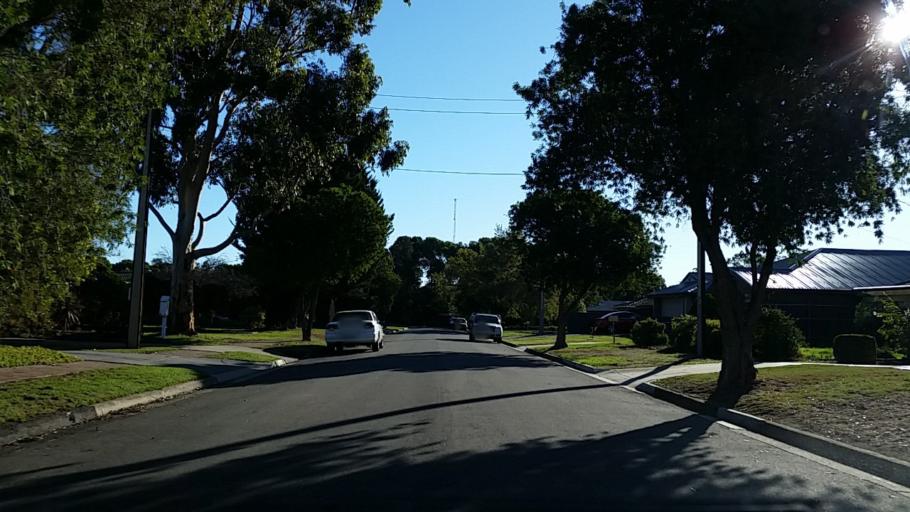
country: AU
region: South Australia
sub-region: Onkaparinga
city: Reynella
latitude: -35.1038
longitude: 138.5312
